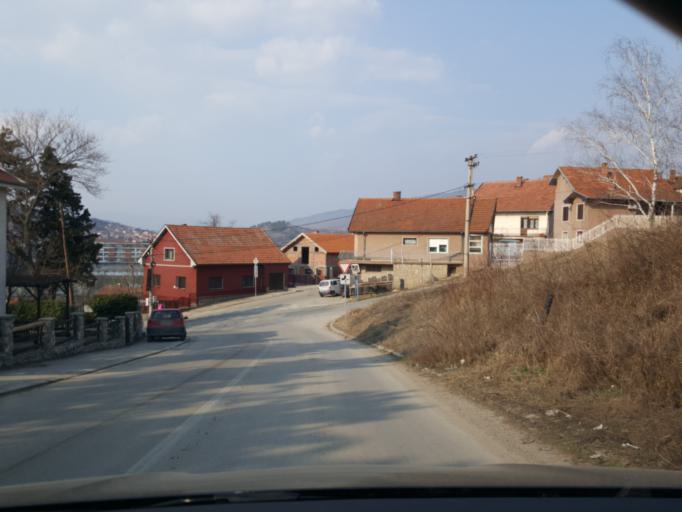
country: RS
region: Central Serbia
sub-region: Nisavski Okrug
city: Aleksinac
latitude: 43.5357
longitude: 21.7129
